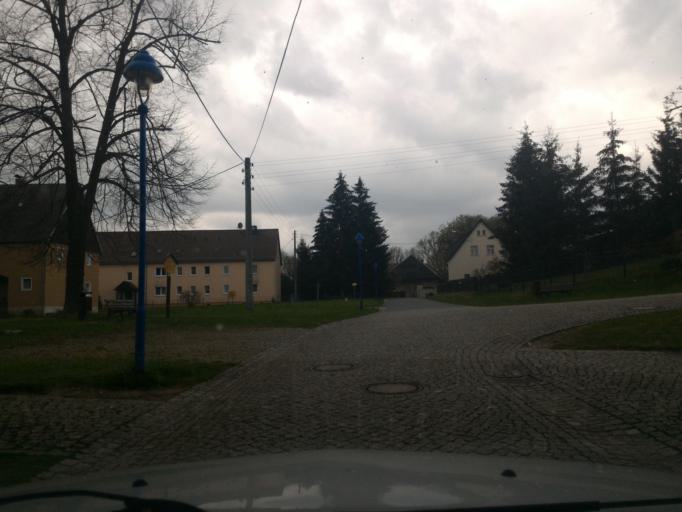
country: DE
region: Saxony
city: Hainewalde
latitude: 50.9158
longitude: 14.7064
